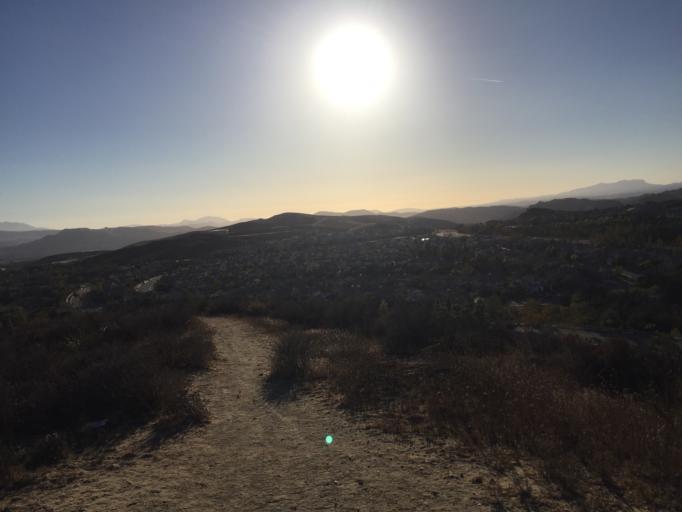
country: US
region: California
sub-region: Ventura County
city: Simi Valley
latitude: 34.2992
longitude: -118.7545
